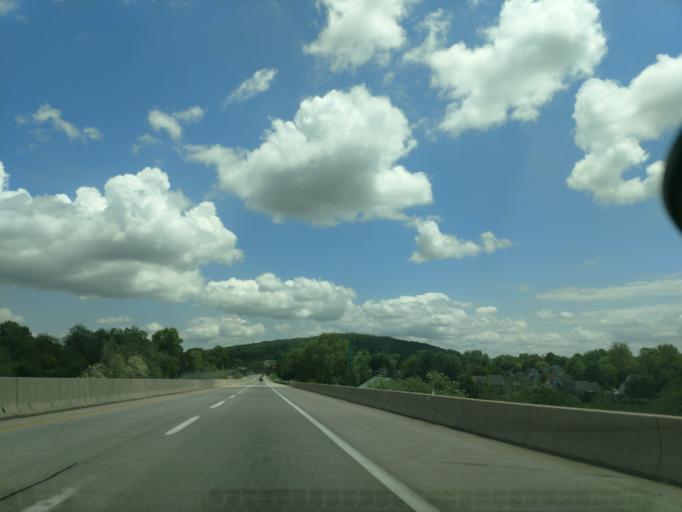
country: US
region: Pennsylvania
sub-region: Lancaster County
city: Denver
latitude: 40.2413
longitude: -76.1427
